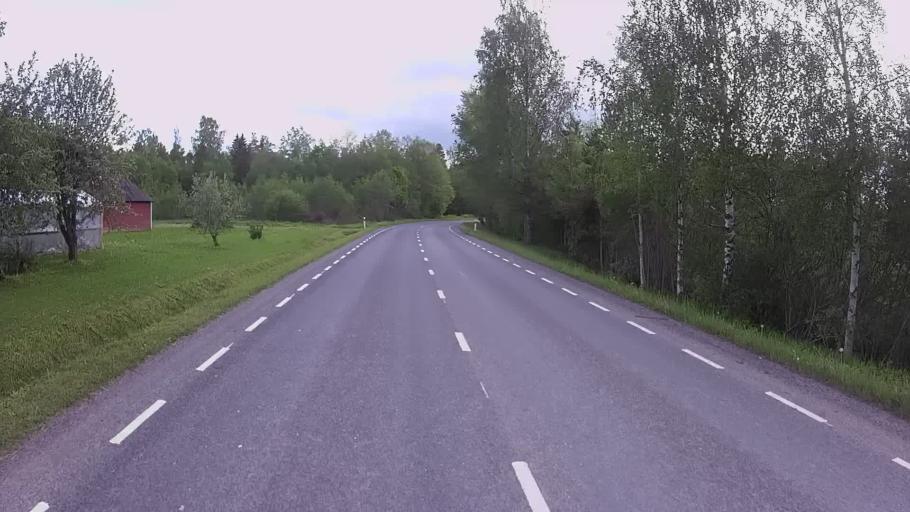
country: EE
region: Jogevamaa
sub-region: Mustvee linn
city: Mustvee
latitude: 58.9844
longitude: 26.8412
